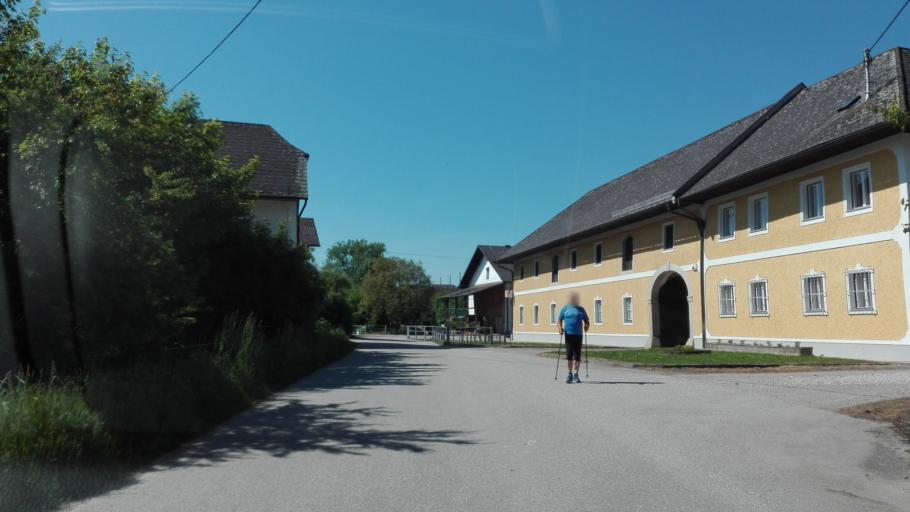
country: AT
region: Upper Austria
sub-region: Politischer Bezirk Urfahr-Umgebung
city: Goldworth
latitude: 48.2794
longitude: 14.0978
